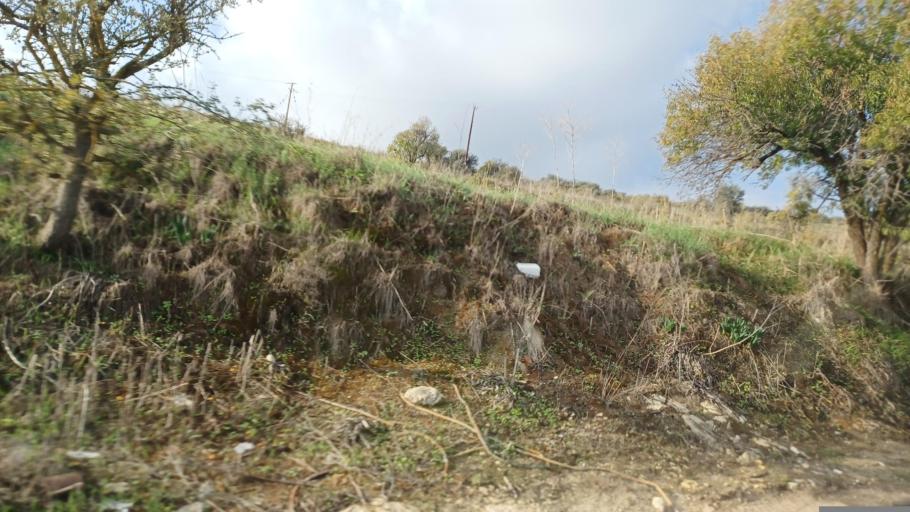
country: CY
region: Pafos
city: Tala
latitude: 34.9102
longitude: 32.4689
